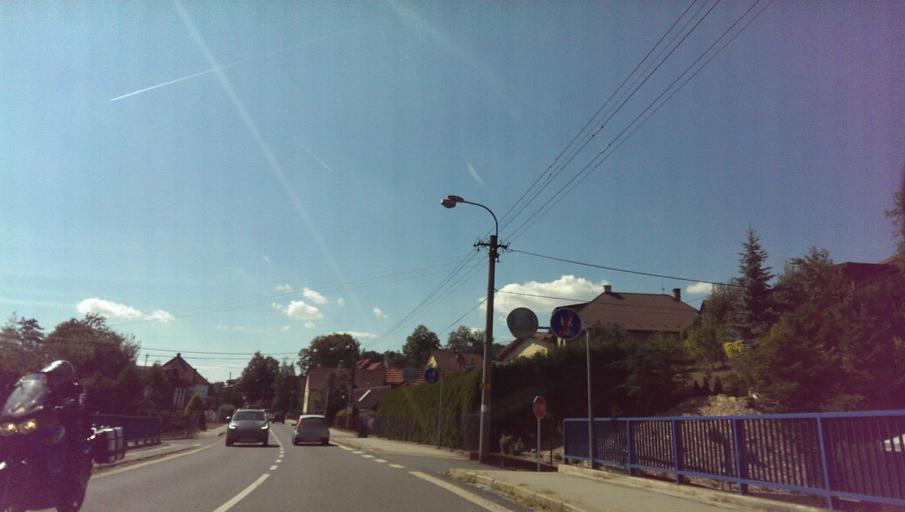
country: CZ
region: Zlin
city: Valasske Mezirici
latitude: 49.4669
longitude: 17.9443
